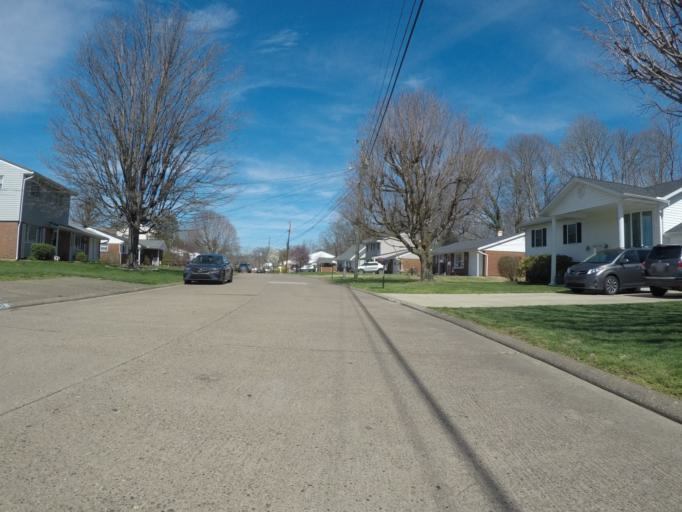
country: US
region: West Virginia
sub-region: Cabell County
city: Pea Ridge
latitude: 38.4003
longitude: -82.3137
